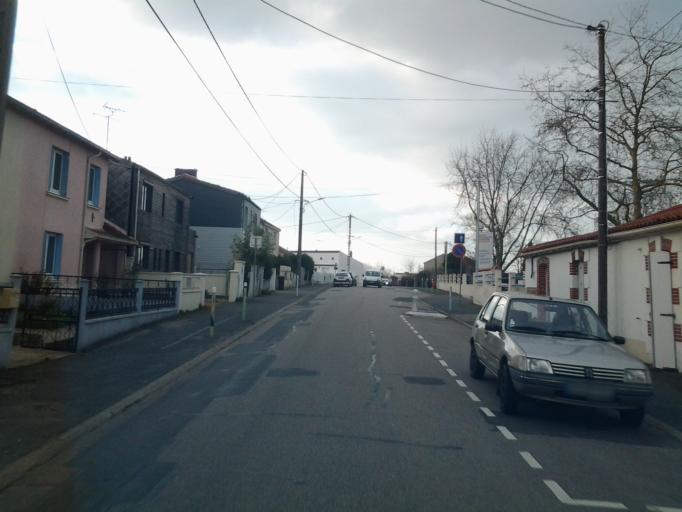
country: FR
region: Pays de la Loire
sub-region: Departement de la Vendee
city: La Roche-sur-Yon
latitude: 46.6855
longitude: -1.4398
